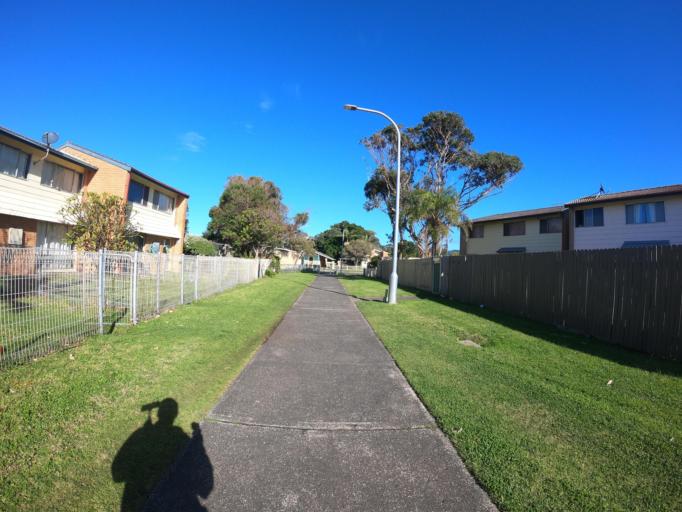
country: AU
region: New South Wales
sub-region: Wollongong
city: East Corrimal
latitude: -34.3665
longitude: 150.9227
